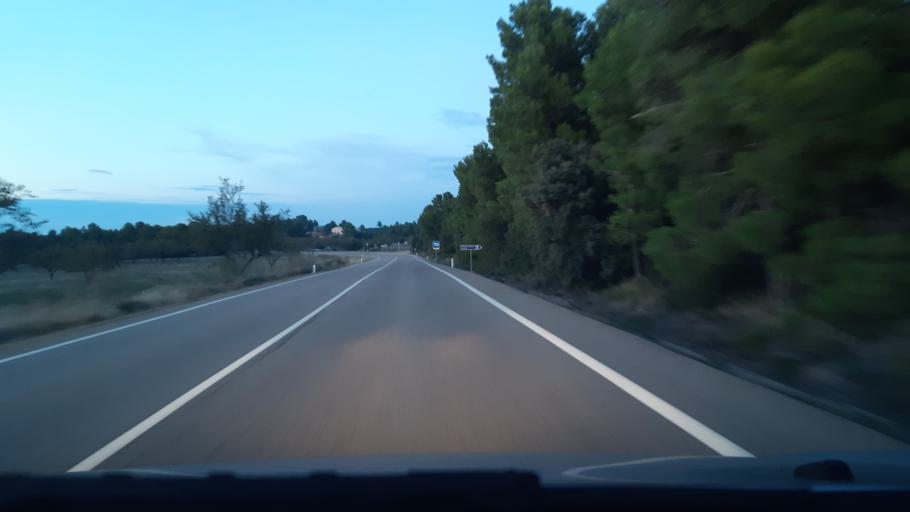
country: ES
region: Aragon
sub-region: Provincia de Teruel
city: Lledo
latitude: 40.9504
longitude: 0.2233
